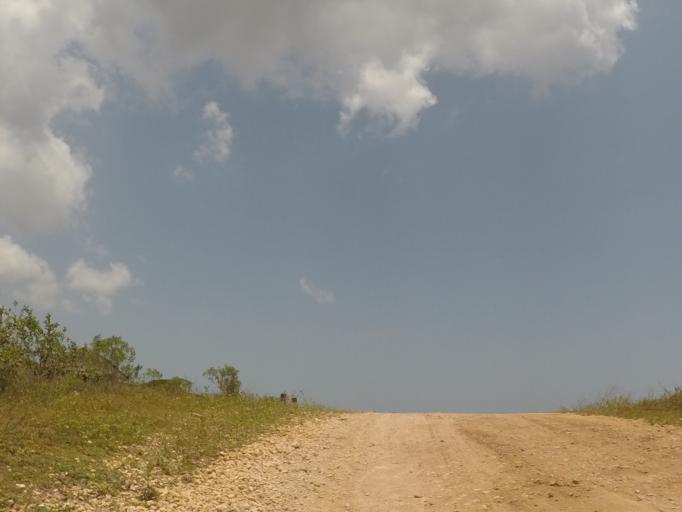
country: TZ
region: Zanzibar Central/South
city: Koani
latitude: -6.1926
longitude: 39.3095
